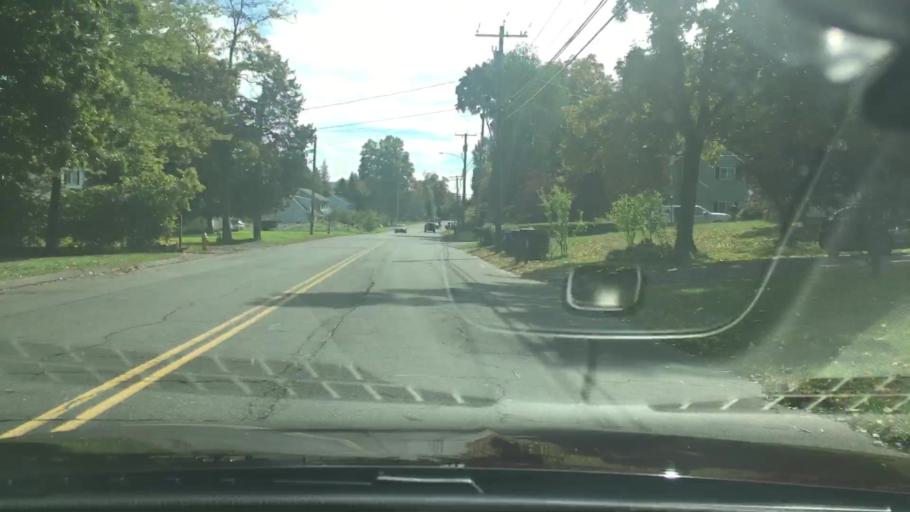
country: US
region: Connecticut
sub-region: Hartford County
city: Plainville
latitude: 41.6535
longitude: -72.8841
